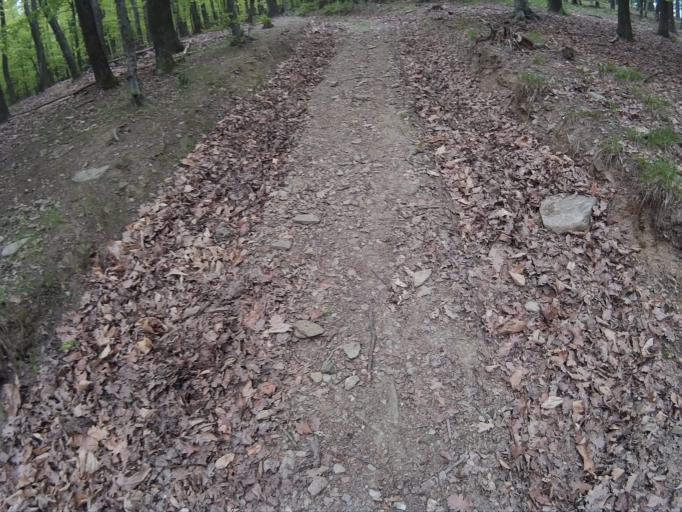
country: HU
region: Vas
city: Koszeg
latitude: 47.3628
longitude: 16.4990
